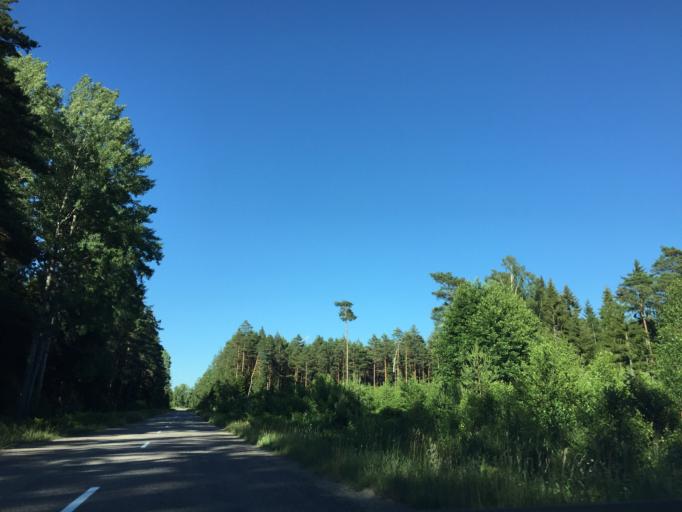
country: LV
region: Ventspils
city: Ventspils
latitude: 57.4883
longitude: 21.7845
